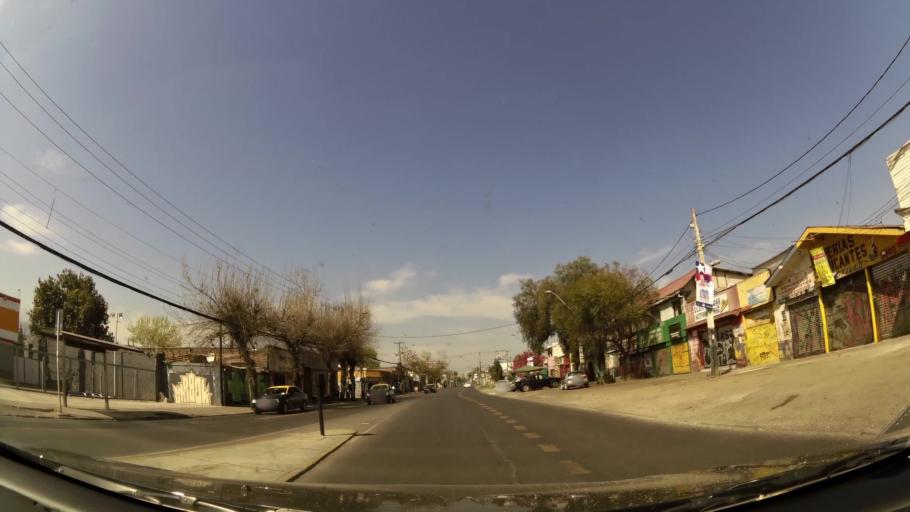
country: CL
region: Santiago Metropolitan
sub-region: Provincia de Santiago
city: Santiago
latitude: -33.3942
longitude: -70.6426
